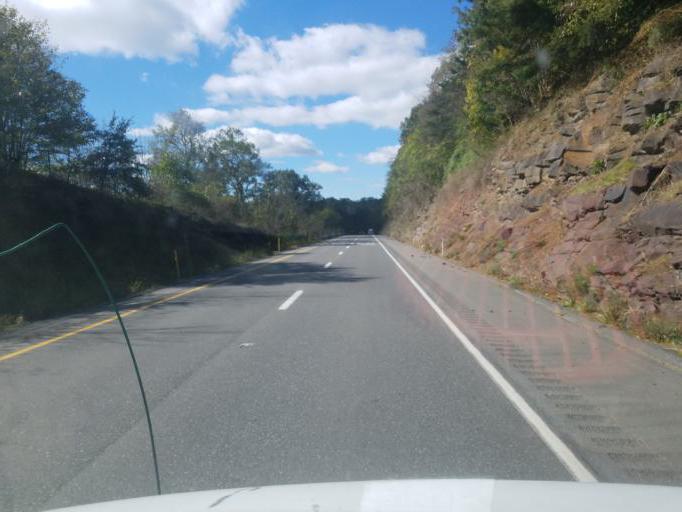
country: US
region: Pennsylvania
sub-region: Bedford County
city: Earlston
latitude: 39.9973
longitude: -78.2556
